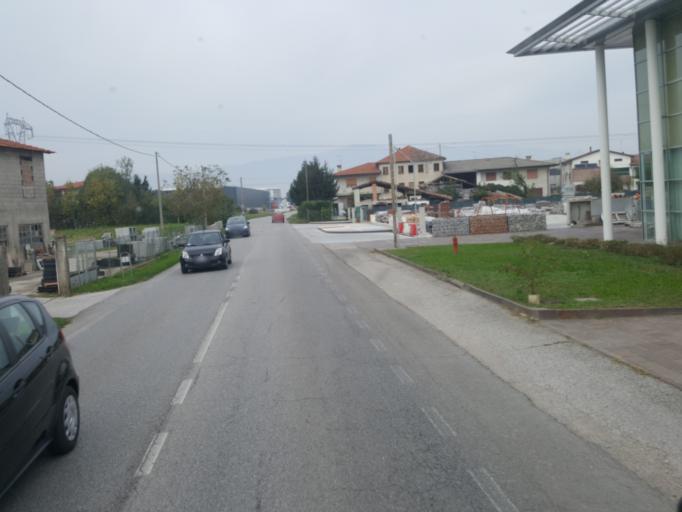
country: IT
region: Veneto
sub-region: Provincia di Treviso
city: Ramon
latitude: 45.7045
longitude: 11.8721
